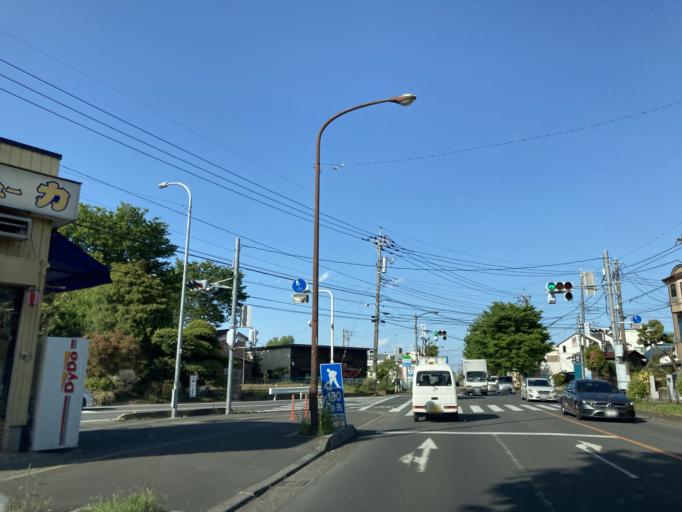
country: JP
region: Saitama
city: Sayama
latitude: 35.8718
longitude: 139.4374
